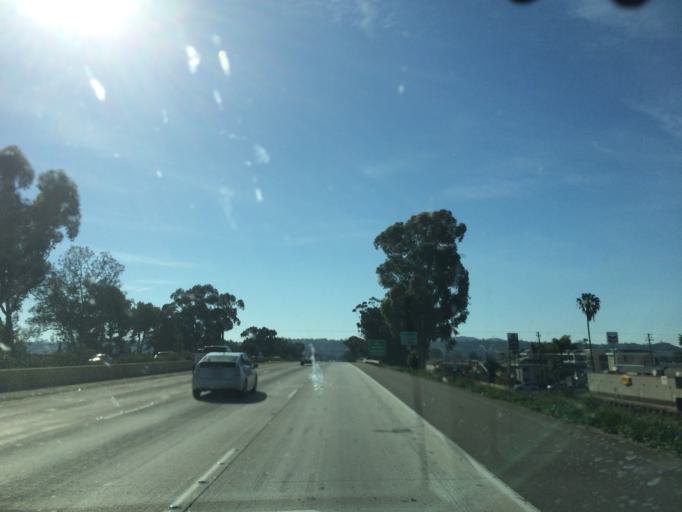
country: US
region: California
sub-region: San Diego County
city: Bostonia
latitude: 32.8032
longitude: -116.9479
